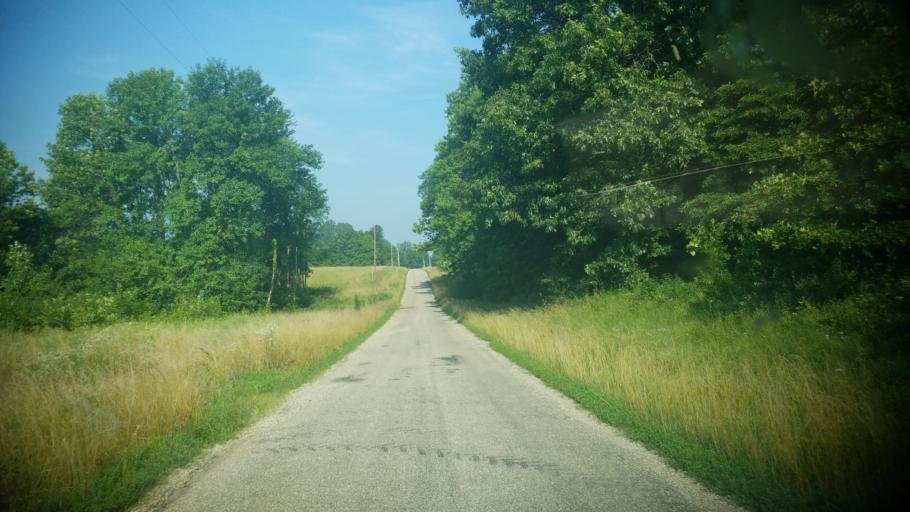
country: US
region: Illinois
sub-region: Clay County
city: Flora
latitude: 38.6028
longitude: -88.4023
